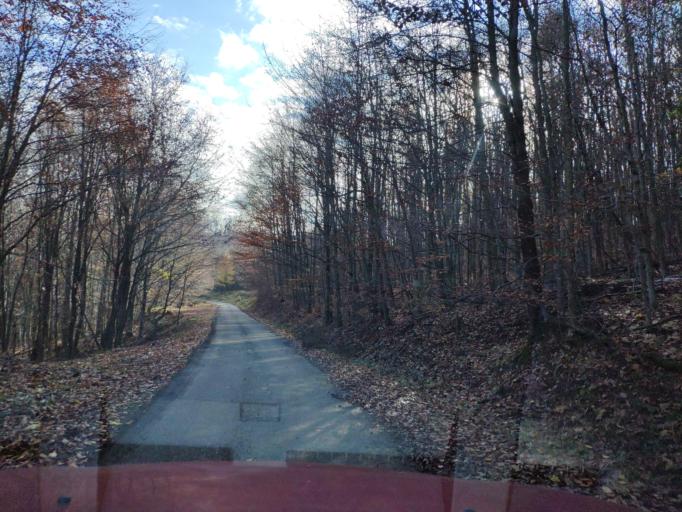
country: SK
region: Kosicky
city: Kosice
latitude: 48.6155
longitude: 21.4560
